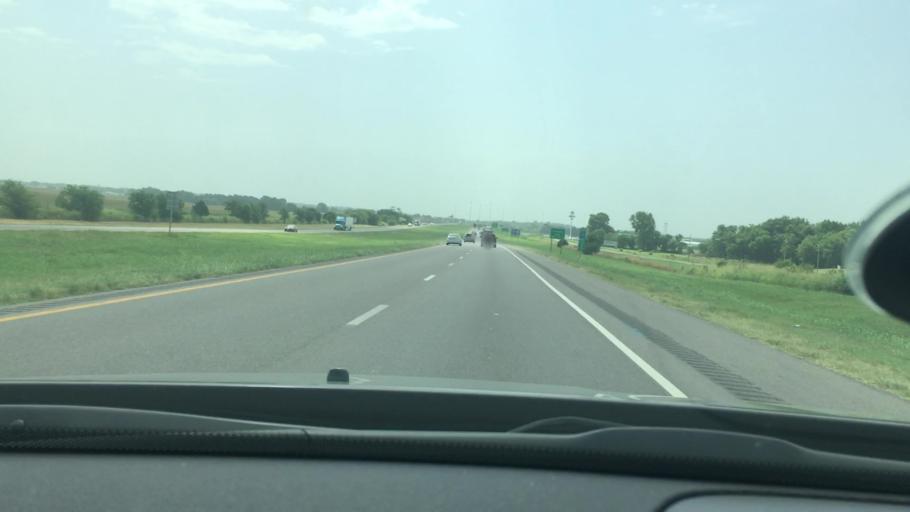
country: US
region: Oklahoma
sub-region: Garvin County
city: Pauls Valley
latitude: 34.7500
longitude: -97.2746
